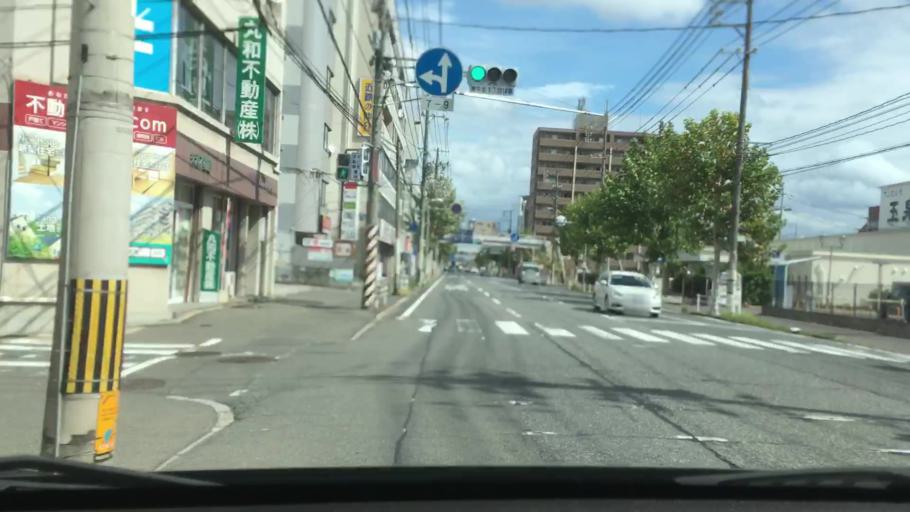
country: JP
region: Hiroshima
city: Hiroshima-shi
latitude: 34.3888
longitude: 132.4198
